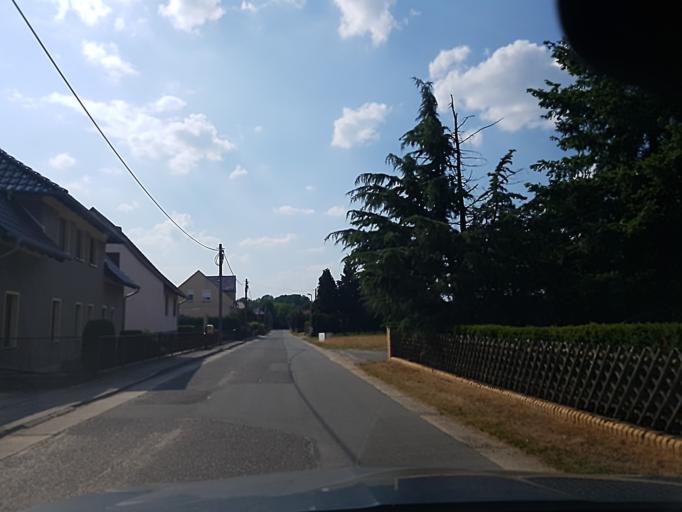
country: DE
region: Brandenburg
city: Bad Liebenwerda
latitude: 51.5330
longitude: 13.4426
